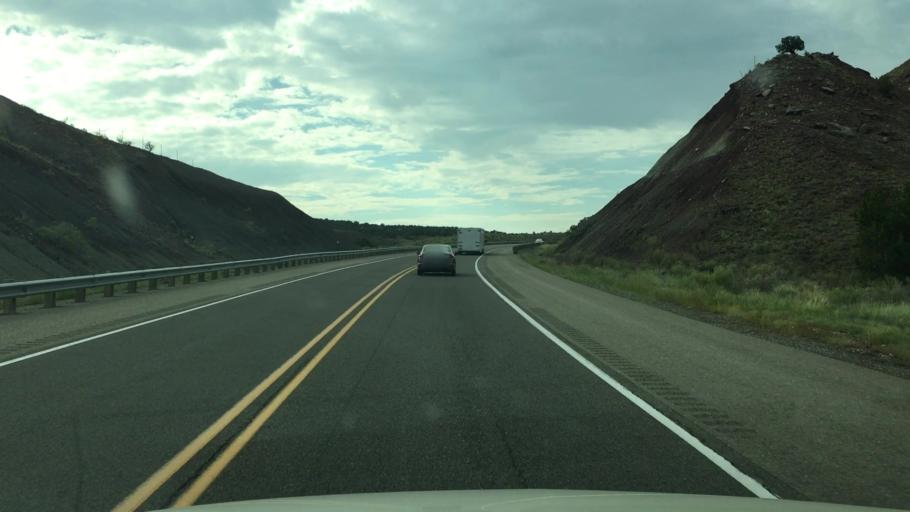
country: US
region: New Mexico
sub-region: Santa Fe County
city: Eldorado at Santa Fe
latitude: 35.2731
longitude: -105.8123
